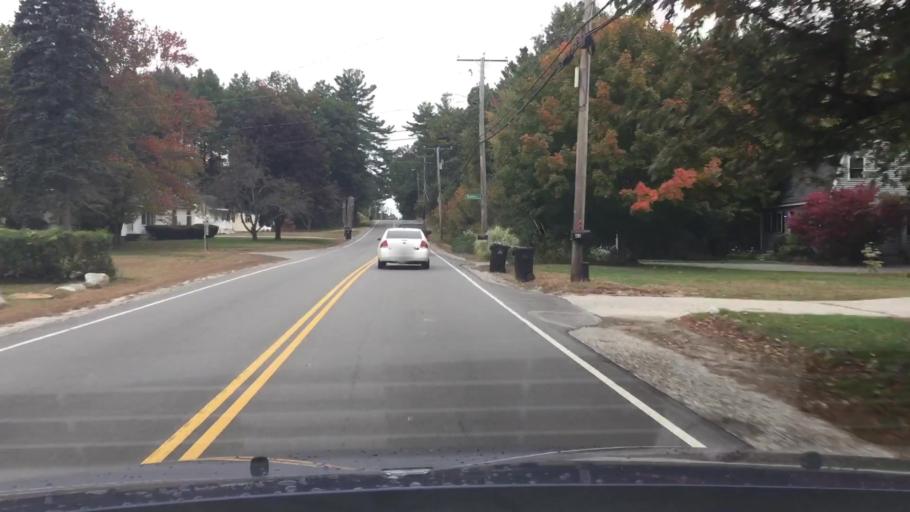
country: US
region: Massachusetts
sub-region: Middlesex County
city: Tyngsboro
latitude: 42.7138
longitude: -71.4109
